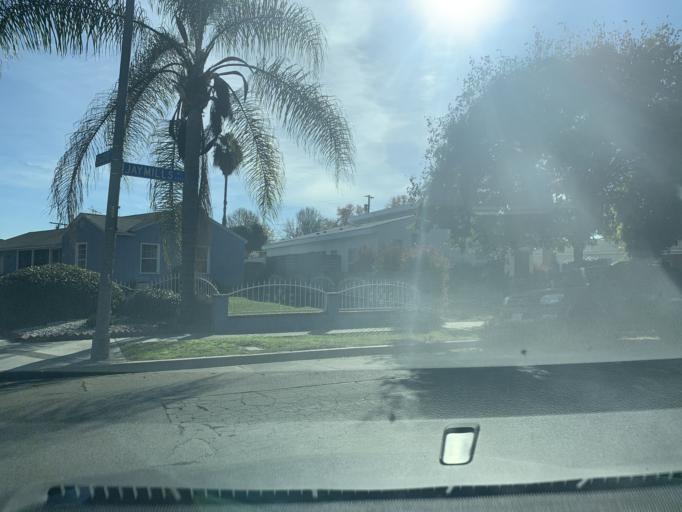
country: US
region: California
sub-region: Los Angeles County
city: East Rancho Dominguez
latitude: 33.8625
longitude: -118.1913
